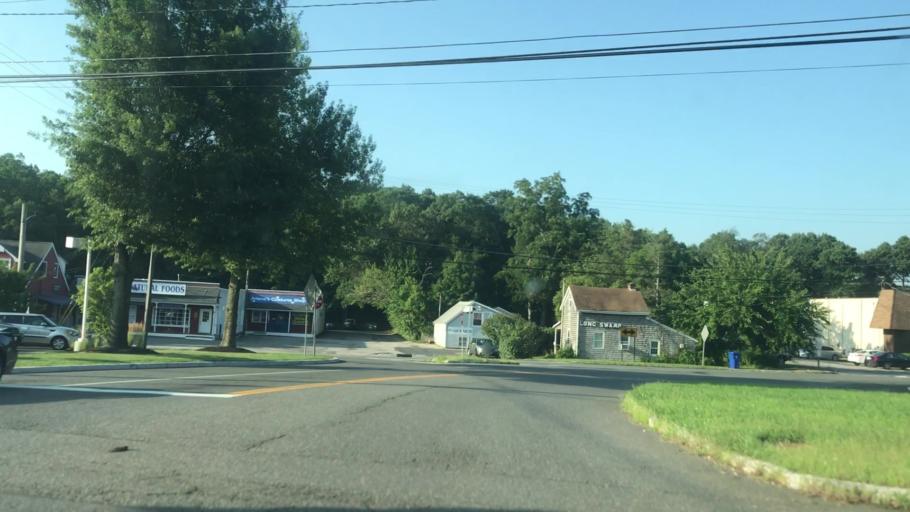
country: US
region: New Jersey
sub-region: Ocean County
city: Pine Beach
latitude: 39.9574
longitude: -74.1702
